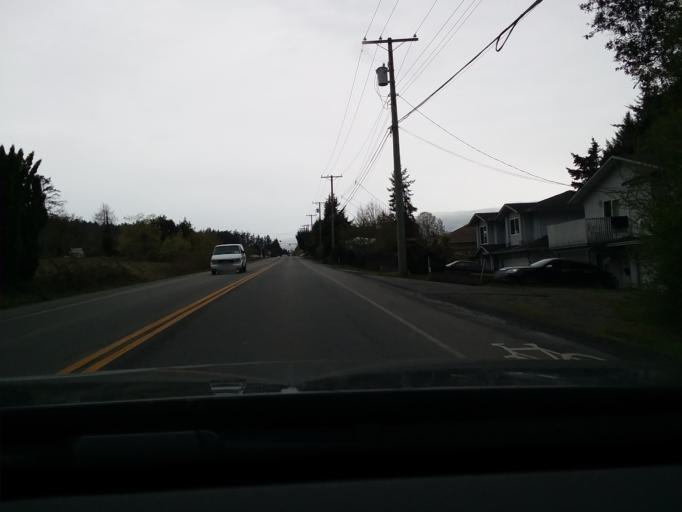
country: CA
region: British Columbia
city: North Saanich
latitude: 48.6300
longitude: -123.4167
